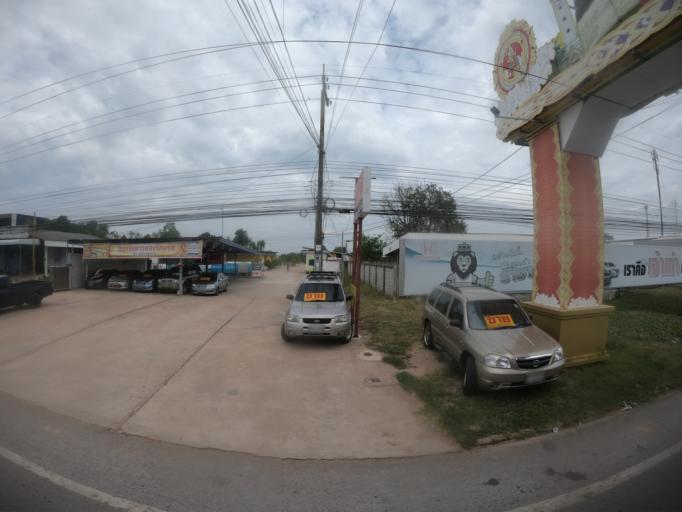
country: TH
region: Maha Sarakham
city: Maha Sarakham
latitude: 16.1653
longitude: 103.3342
